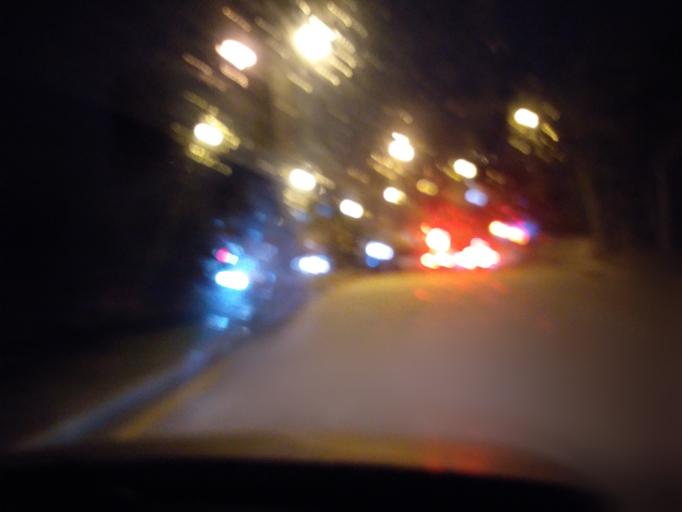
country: TR
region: Ankara
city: Batikent
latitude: 39.8803
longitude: 32.7119
